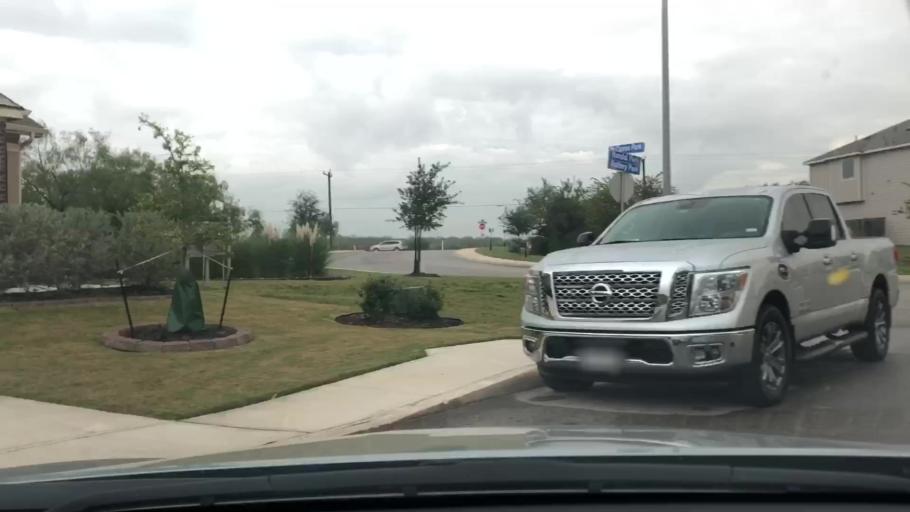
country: US
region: Texas
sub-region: Bexar County
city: Converse
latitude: 29.4686
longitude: -98.3088
